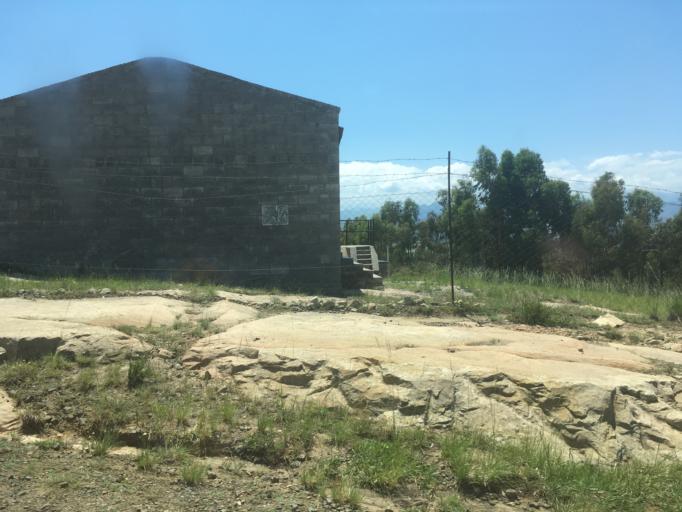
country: LS
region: Butha-Buthe
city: Butha-Buthe
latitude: -28.7220
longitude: 28.3591
